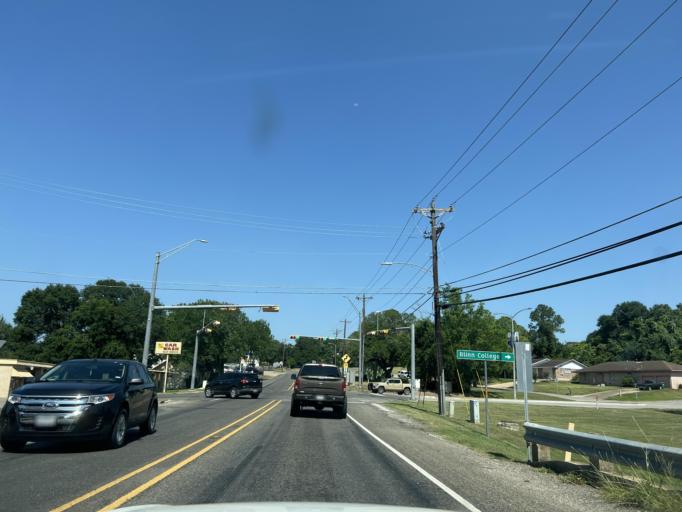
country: US
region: Texas
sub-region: Washington County
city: Brenham
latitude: 30.1652
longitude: -96.4116
